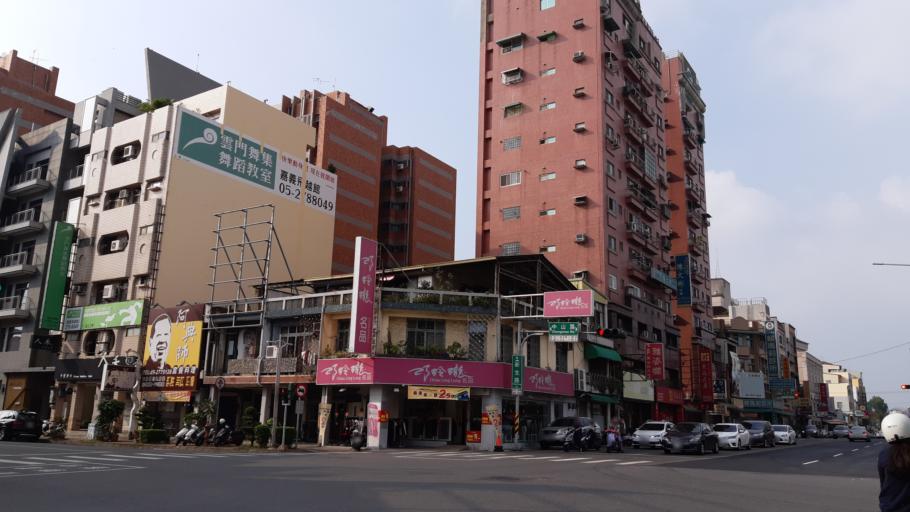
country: TW
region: Taiwan
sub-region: Chiayi
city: Jiayi Shi
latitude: 23.4824
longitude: 120.4612
